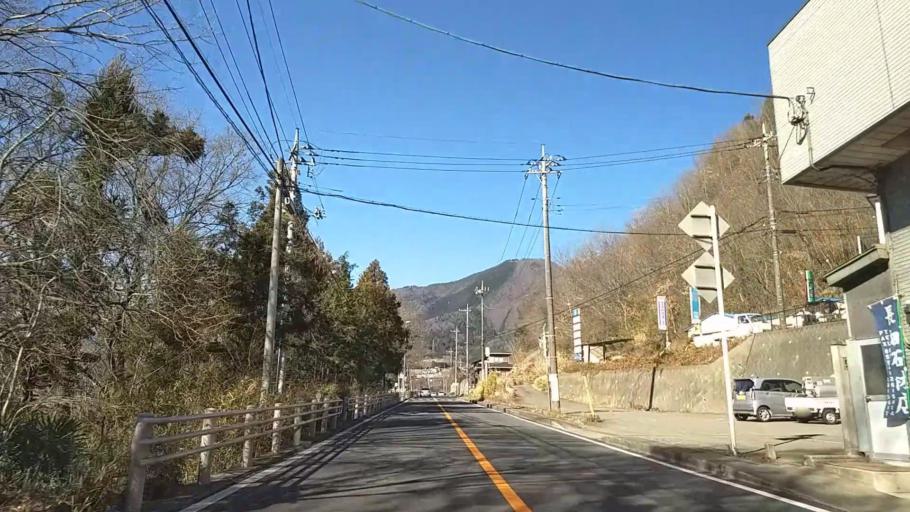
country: JP
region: Yamanashi
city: Otsuki
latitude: 35.6110
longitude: 138.9957
